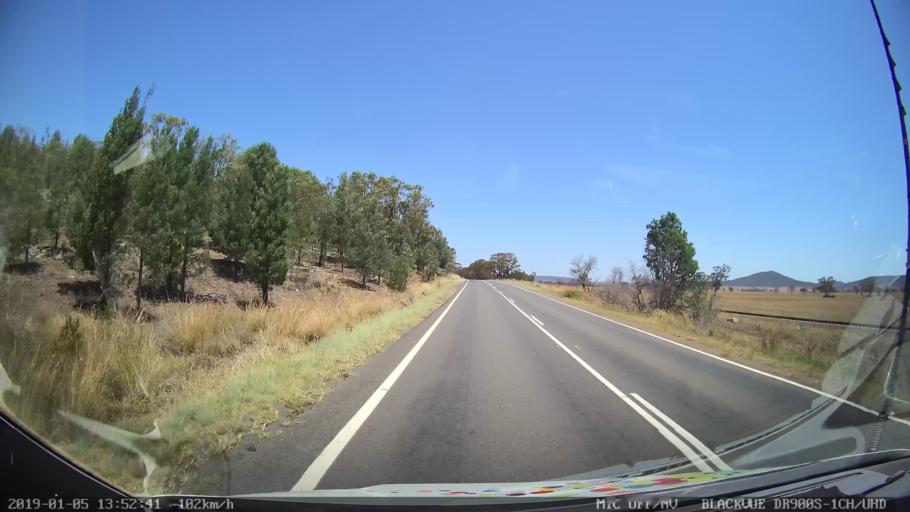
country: AU
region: New South Wales
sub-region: Gunnedah
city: Gunnedah
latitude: -31.0636
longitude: 150.2769
